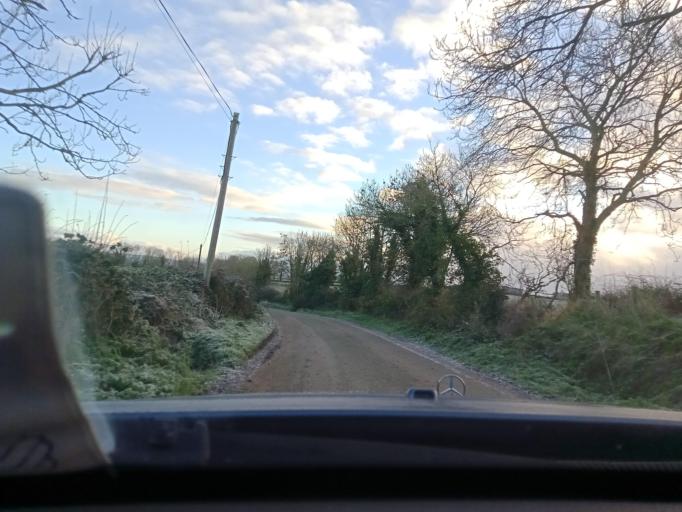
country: IE
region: Leinster
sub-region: County Carlow
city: Bagenalstown
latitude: 52.6383
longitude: -7.0292
